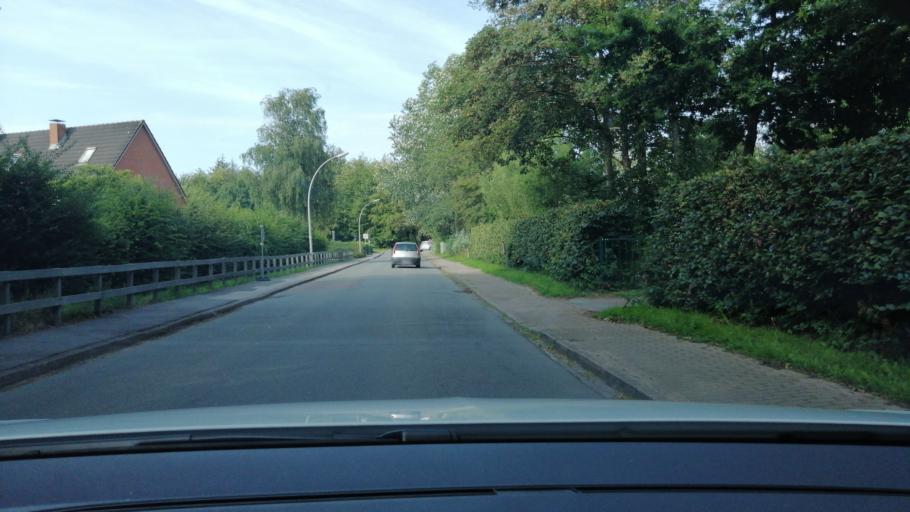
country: DE
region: Schleswig-Holstein
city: Leck
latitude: 54.7737
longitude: 8.9617
